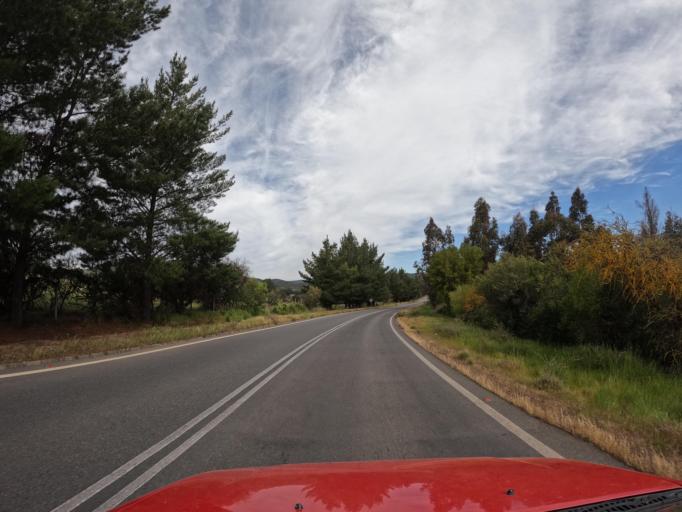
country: CL
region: Maule
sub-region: Provincia de Talca
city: Talca
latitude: -35.3314
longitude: -71.9263
